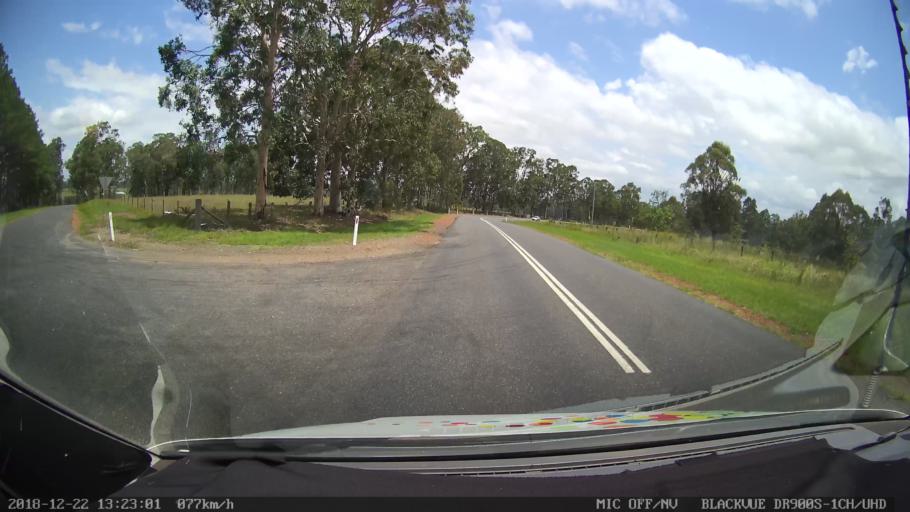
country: AU
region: New South Wales
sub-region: Clarence Valley
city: Coutts Crossing
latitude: -29.7936
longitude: 152.9097
